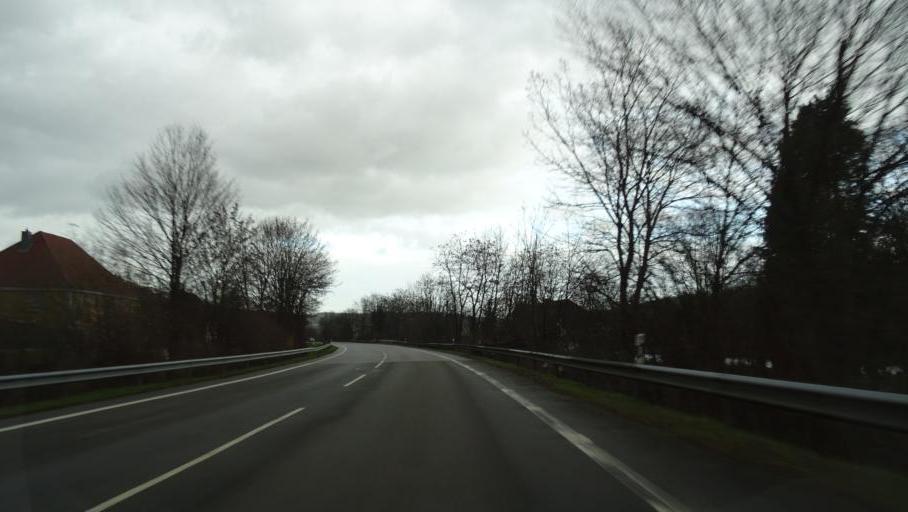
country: DE
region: Baden-Wuerttemberg
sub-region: Karlsruhe Region
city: Binau
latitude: 49.3650
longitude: 9.0561
